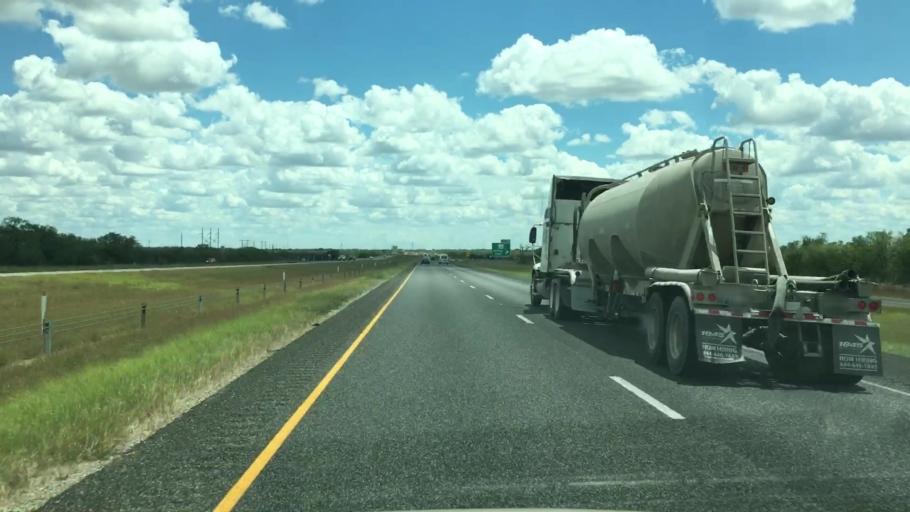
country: US
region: Texas
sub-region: Atascosa County
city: Pleasanton
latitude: 28.8505
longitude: -98.3814
